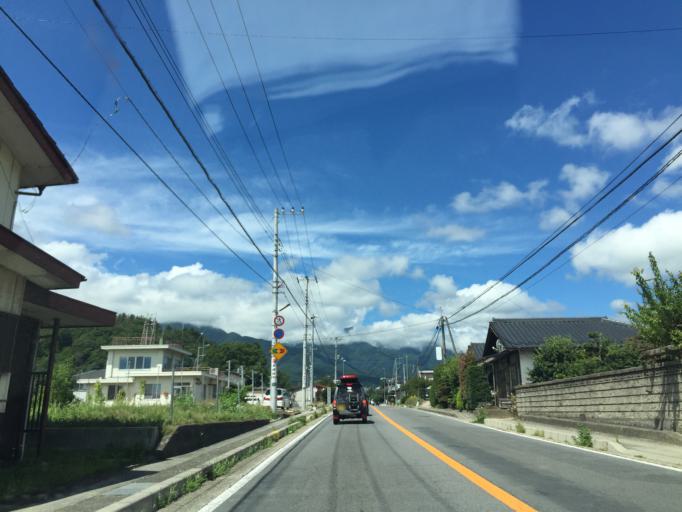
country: JP
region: Yamanashi
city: Nirasaki
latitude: 35.8064
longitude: 138.3495
